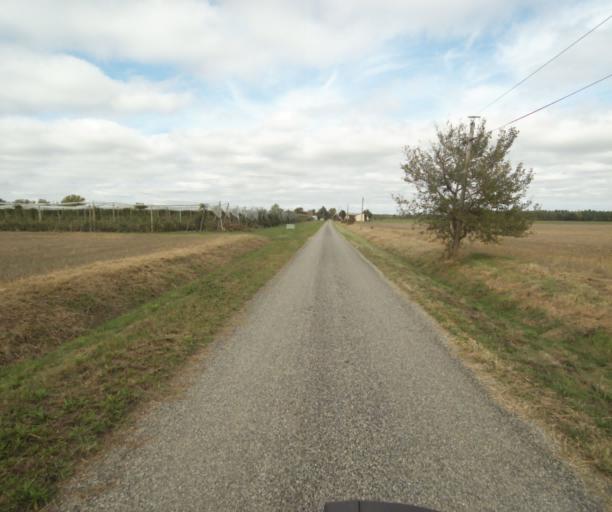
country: FR
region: Midi-Pyrenees
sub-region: Departement du Tarn-et-Garonne
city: Finhan
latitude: 43.9312
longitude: 1.2062
